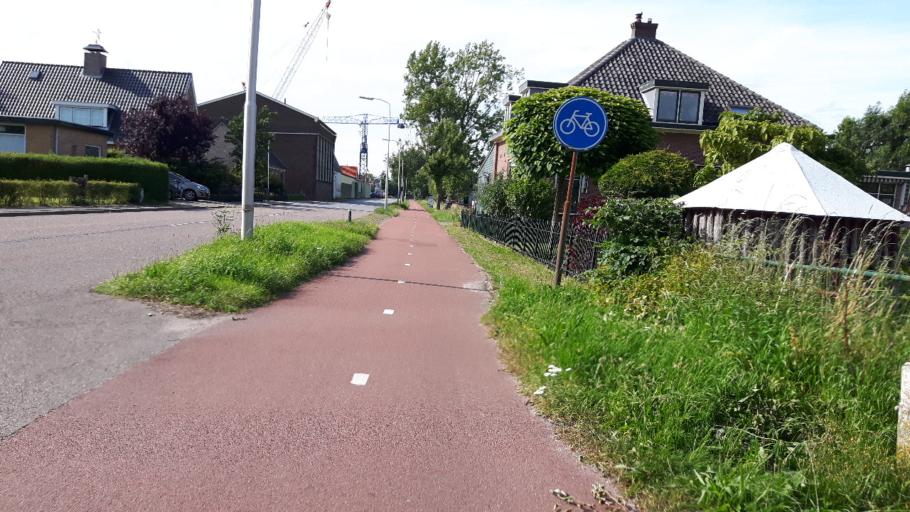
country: NL
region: South Holland
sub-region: Gemeente Delft
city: Delft
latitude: 51.9786
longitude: 4.3821
